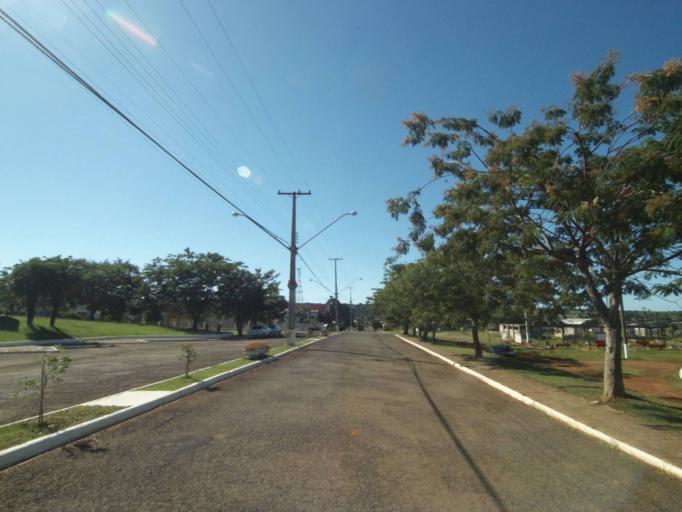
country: BR
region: Parana
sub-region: Pinhao
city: Pinhao
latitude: -25.8347
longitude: -52.0308
